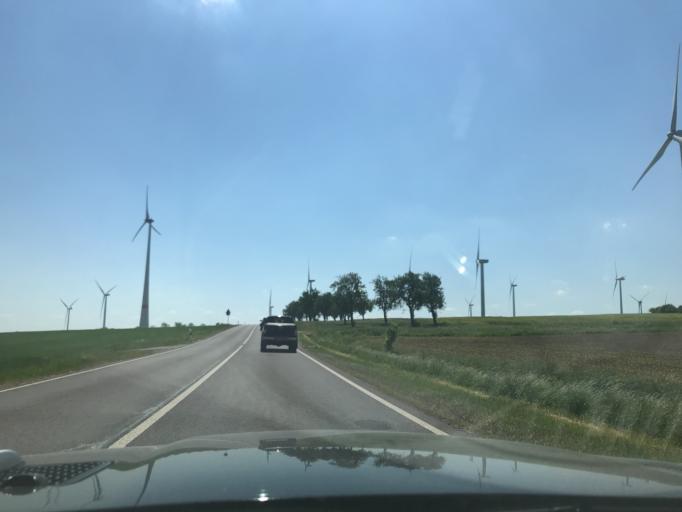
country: DE
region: Thuringia
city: Hochheim
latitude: 51.0435
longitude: 10.6611
